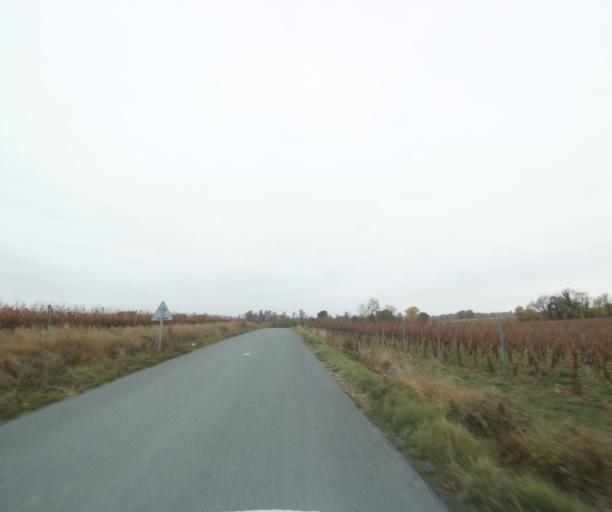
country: FR
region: Poitou-Charentes
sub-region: Departement de la Charente-Maritime
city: Chermignac
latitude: 45.7138
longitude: -0.6800
